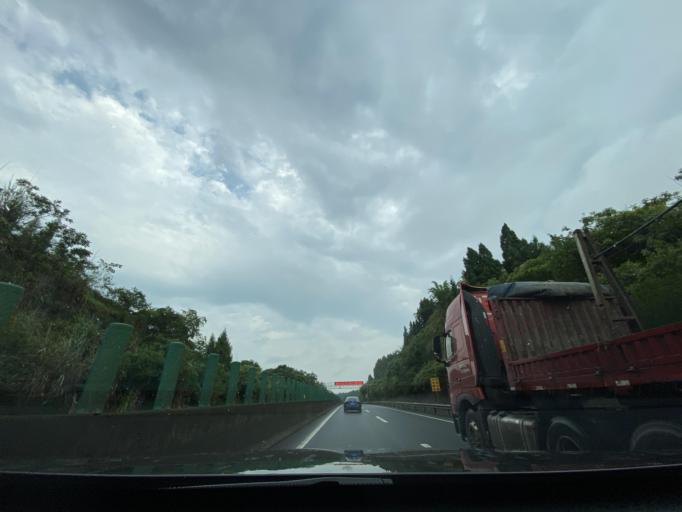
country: CN
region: Sichuan
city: Yanjiang
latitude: 30.1152
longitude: 104.6000
